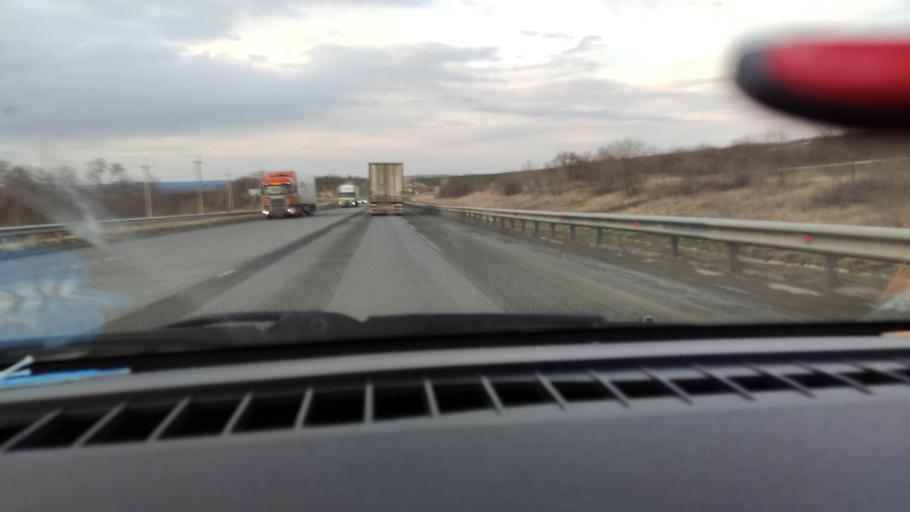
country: RU
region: Saratov
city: Shumeyka
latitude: 51.7841
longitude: 46.1328
